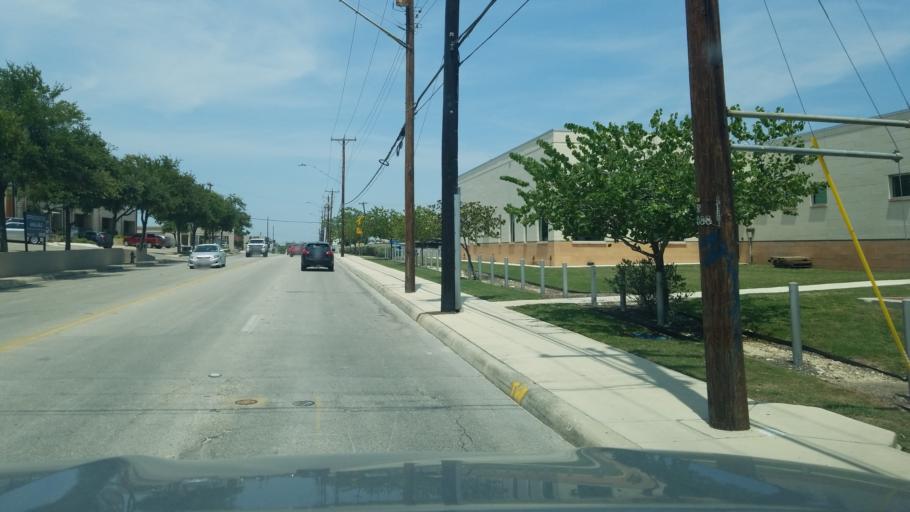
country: US
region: Texas
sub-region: Bexar County
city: Castle Hills
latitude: 29.5261
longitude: -98.4954
